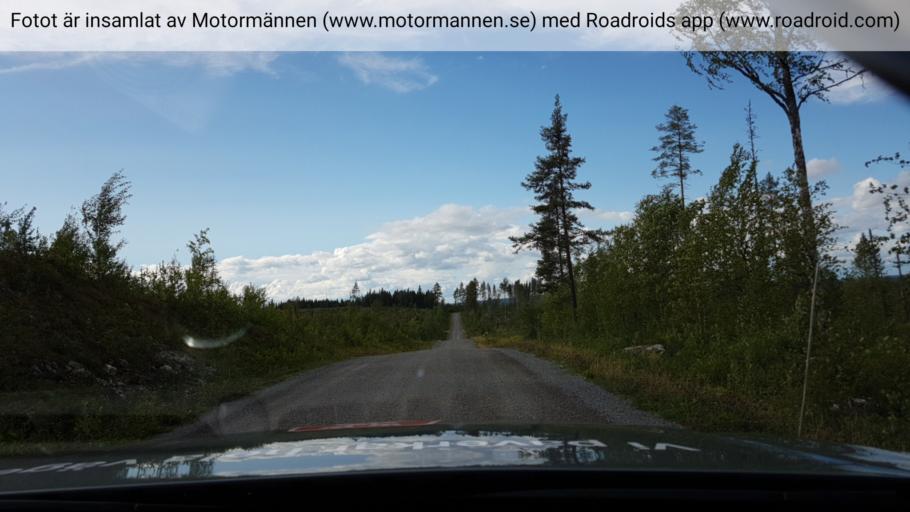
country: SE
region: Jaemtland
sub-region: OEstersunds Kommun
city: Lit
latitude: 63.2941
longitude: 15.3389
